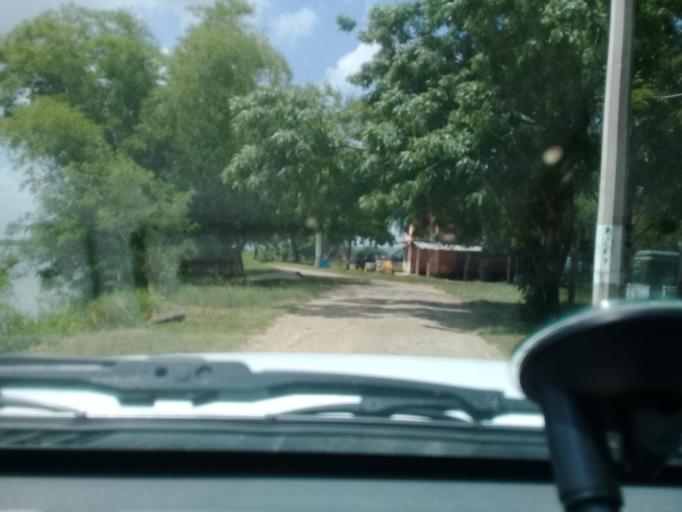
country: MX
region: Veracruz
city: Moralillo
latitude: 22.1755
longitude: -98.0165
